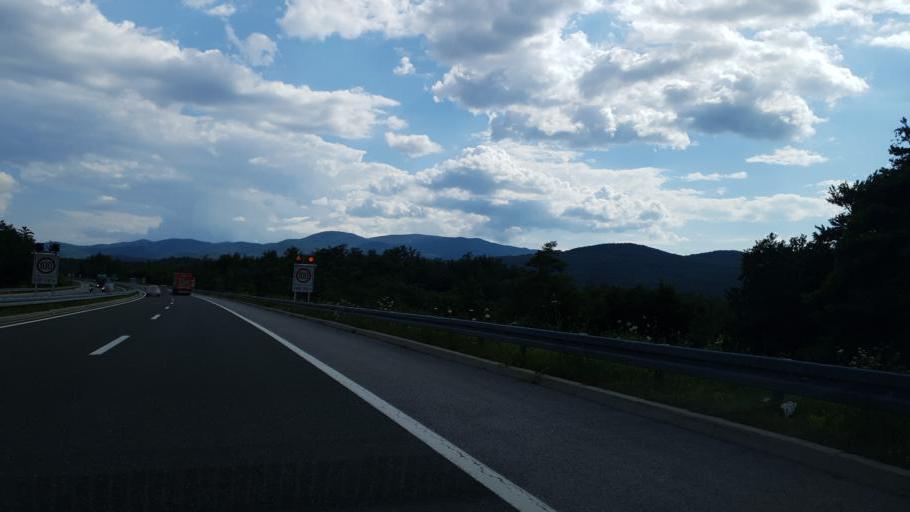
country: HR
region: Primorsko-Goranska
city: Klana
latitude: 45.4630
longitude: 14.2692
